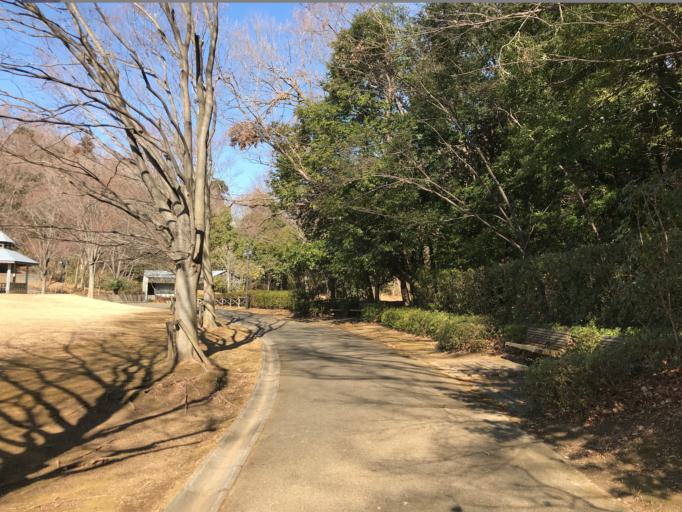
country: JP
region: Tokyo
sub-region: Machida-shi
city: Machida
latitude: 35.6081
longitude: 139.4661
